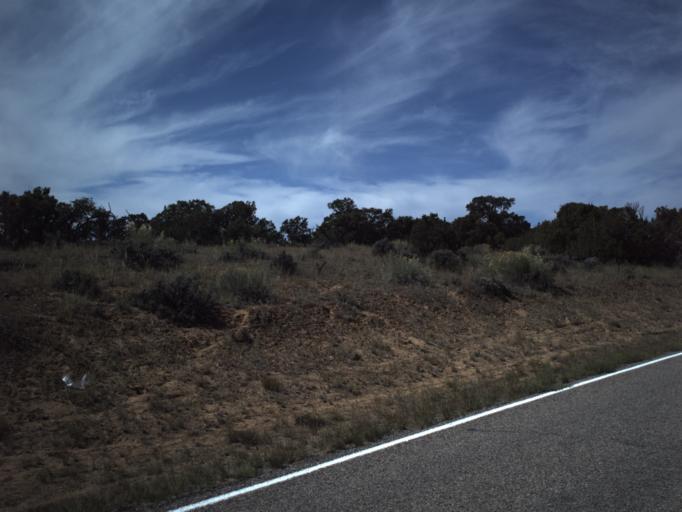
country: US
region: Utah
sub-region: Wayne County
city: Loa
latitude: 37.8720
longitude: -111.4449
